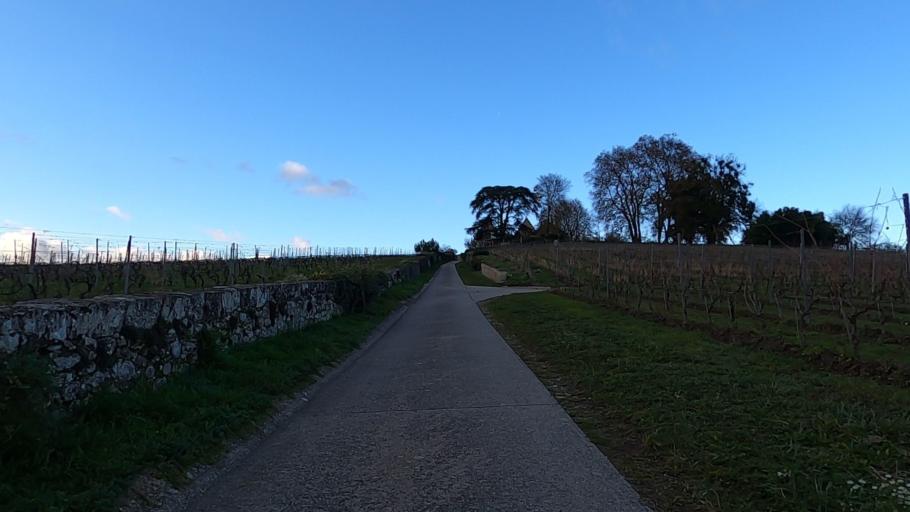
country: CH
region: Vaud
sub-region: Morges District
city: Saint-Prex
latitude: 46.5159
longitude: 6.4608
